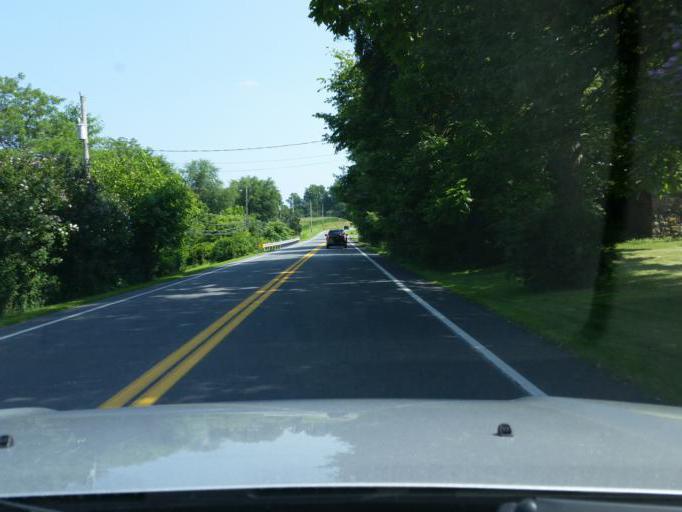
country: US
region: Pennsylvania
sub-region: Dauphin County
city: Hershey
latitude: 40.2521
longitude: -76.6276
